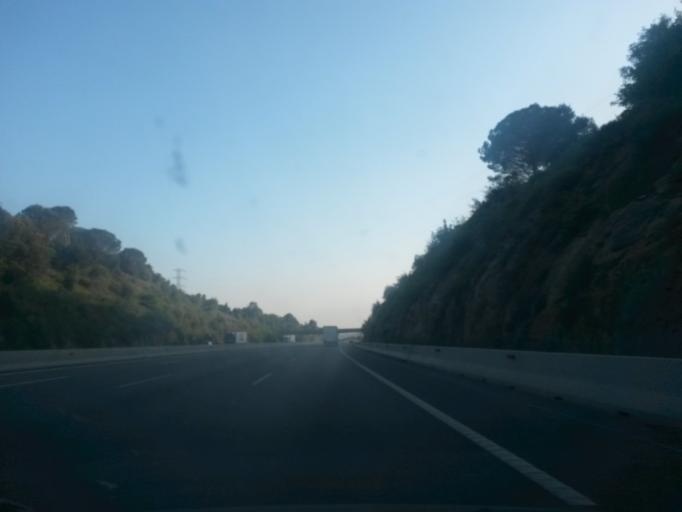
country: ES
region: Catalonia
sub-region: Provincia de Girona
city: Girona
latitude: 42.0038
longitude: 2.8061
